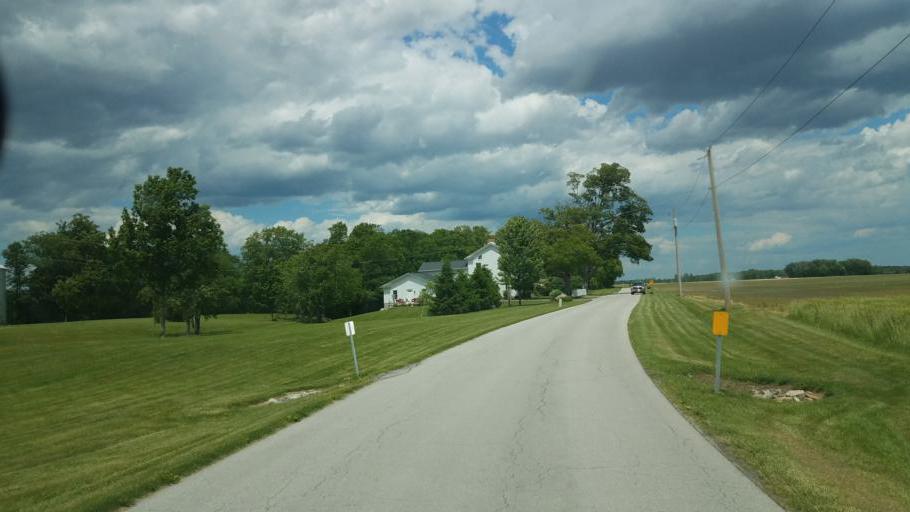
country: US
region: Ohio
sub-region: Huron County
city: Monroeville
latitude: 41.2730
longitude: -82.6765
